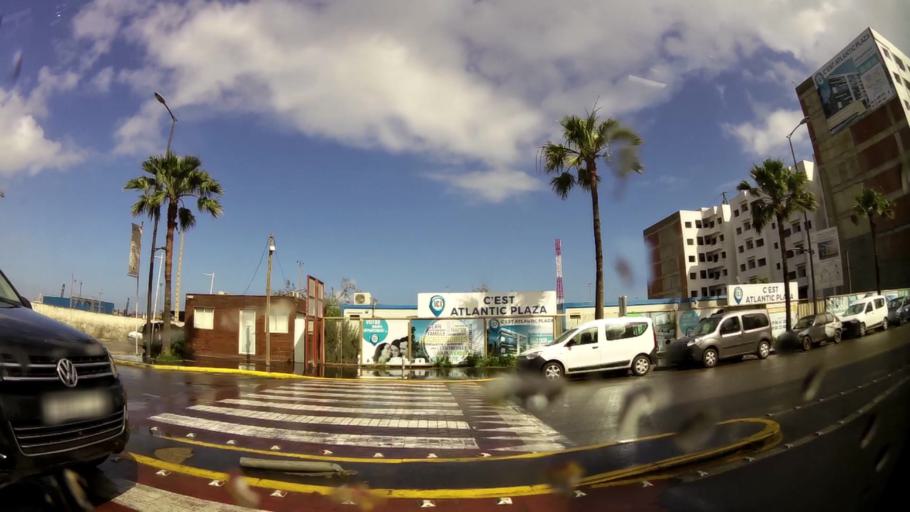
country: MA
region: Grand Casablanca
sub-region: Casablanca
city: Casablanca
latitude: 33.6001
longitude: -7.5887
